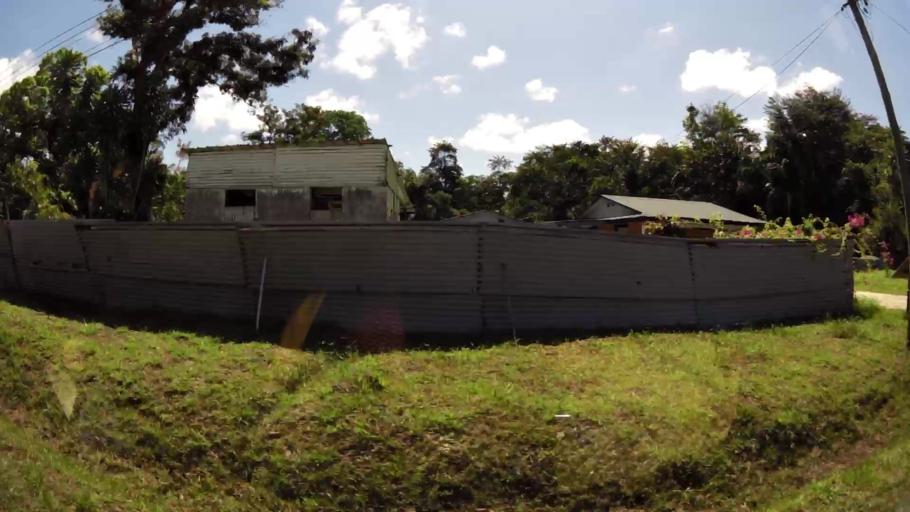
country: GF
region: Guyane
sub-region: Guyane
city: Matoury
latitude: 4.8448
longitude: -52.3297
